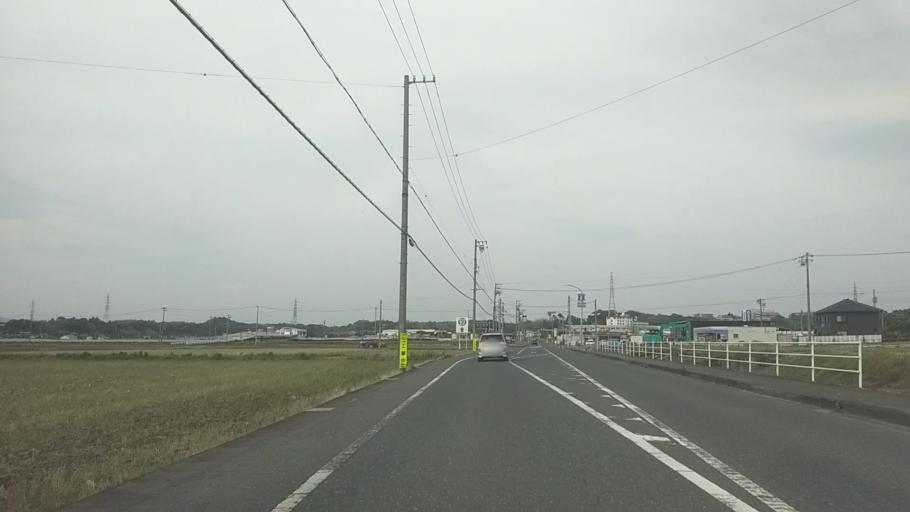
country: JP
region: Shizuoka
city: Hamamatsu
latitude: 34.7378
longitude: 137.6458
